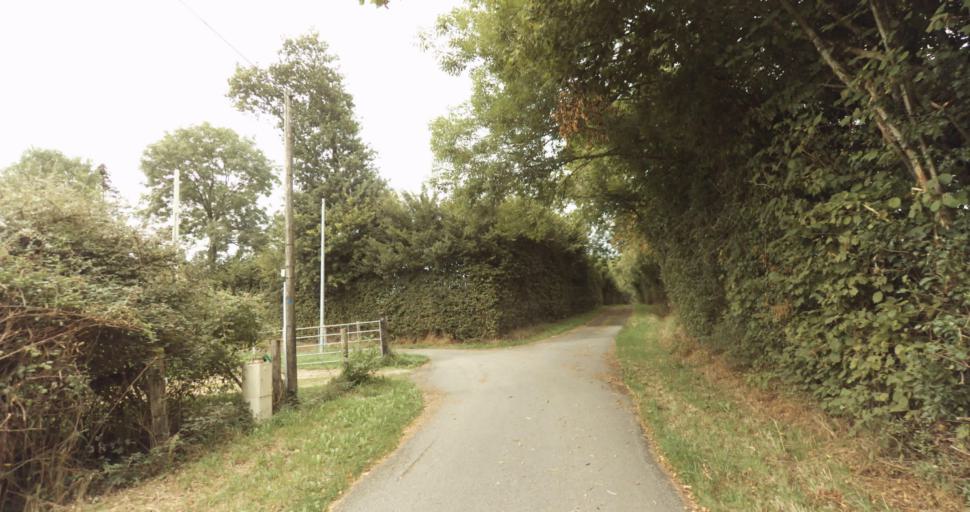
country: FR
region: Lower Normandy
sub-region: Departement de l'Orne
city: Gace
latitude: 48.6737
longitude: 0.3112
